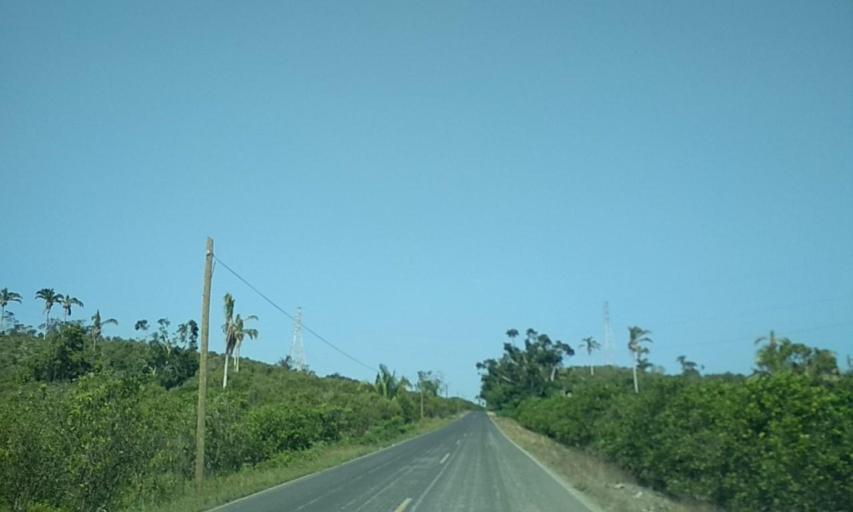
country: MX
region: Veracruz
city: Gutierrez Zamora
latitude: 20.3539
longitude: -97.1548
